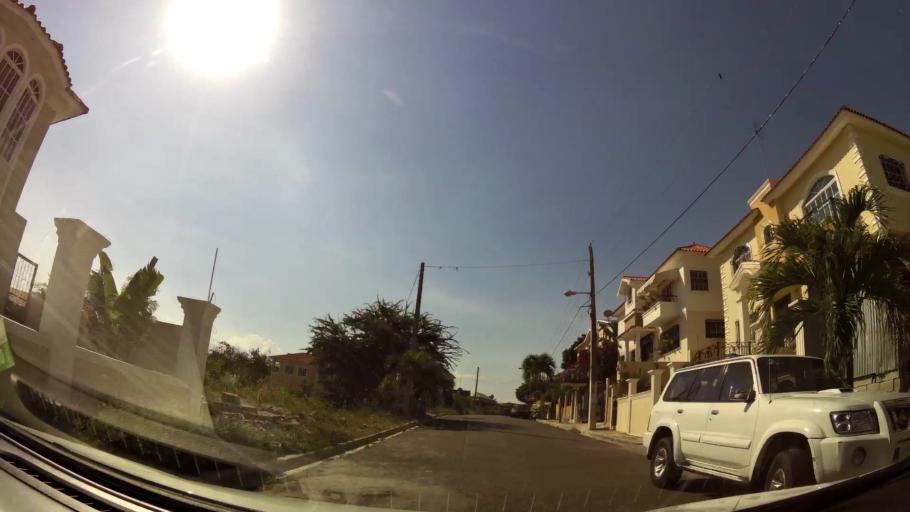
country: DO
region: Nacional
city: Bella Vista
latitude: 18.4601
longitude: -69.9814
